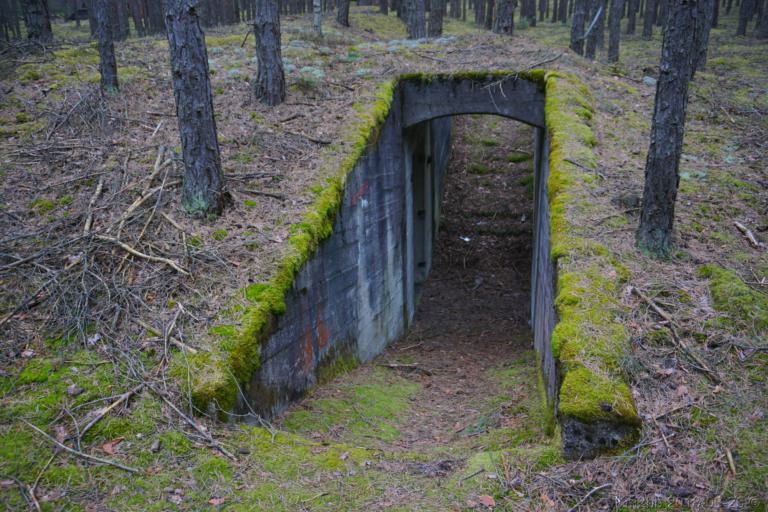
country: PL
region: Lubusz
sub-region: Powiat zielonogorski
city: Nowogrod Bobrzanski
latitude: 51.8038
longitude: 15.1927
